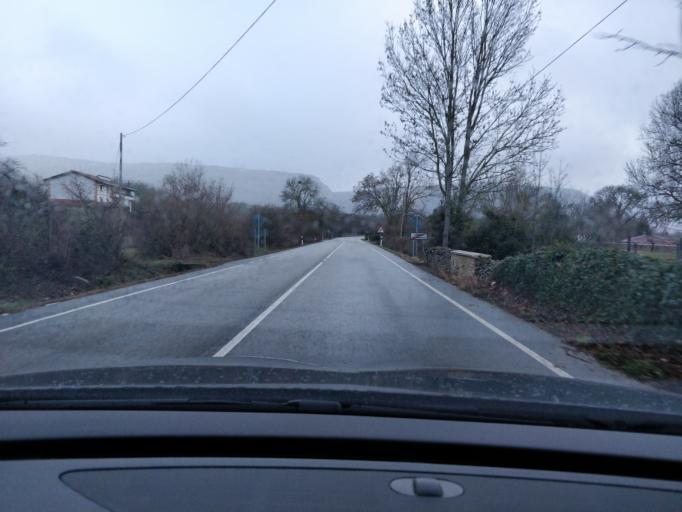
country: ES
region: Castille and Leon
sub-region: Provincia de Burgos
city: Espinosa de los Monteros
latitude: 43.0605
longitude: -3.4944
